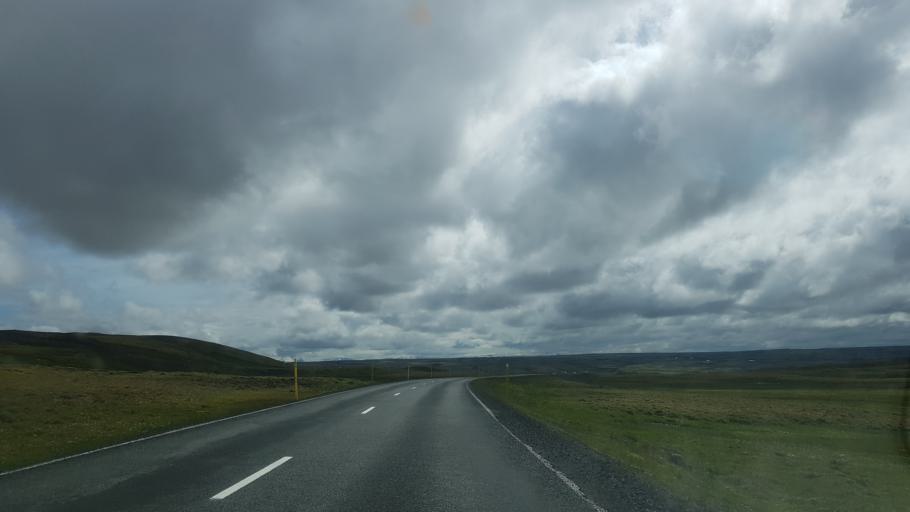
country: IS
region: West
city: Borgarnes
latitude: 64.9635
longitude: -21.0615
